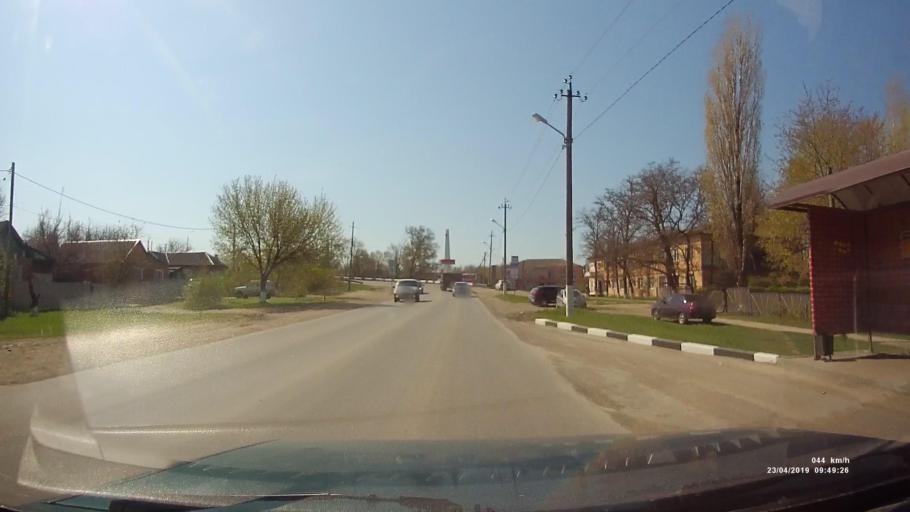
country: RU
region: Rostov
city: Orlovskiy
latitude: 46.8656
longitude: 42.0343
